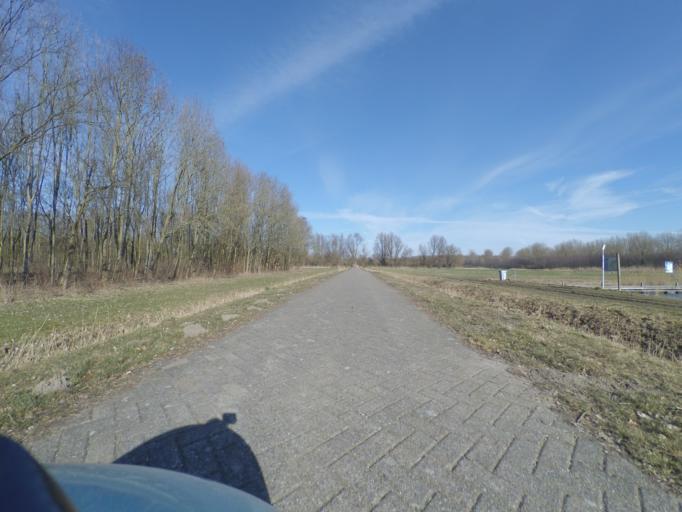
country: NL
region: Flevoland
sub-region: Gemeente Almere
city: Almere Stad
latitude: 52.4031
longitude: 5.2256
